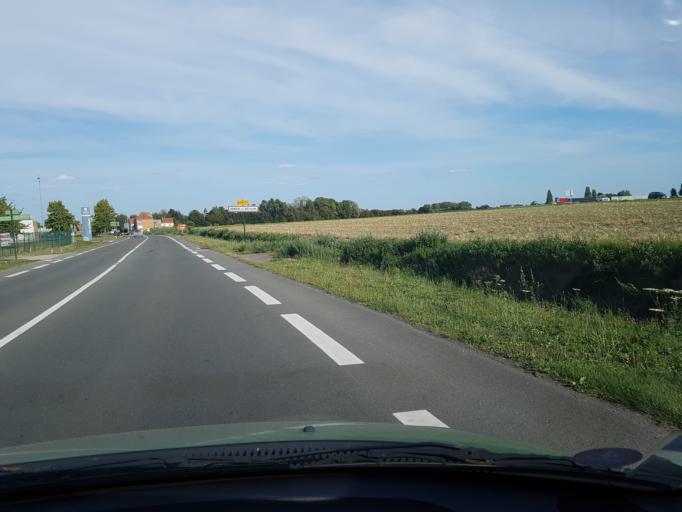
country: FR
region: Nord-Pas-de-Calais
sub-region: Departement du Pas-de-Calais
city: Vendin-les-Bethune
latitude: 50.5390
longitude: 2.5921
